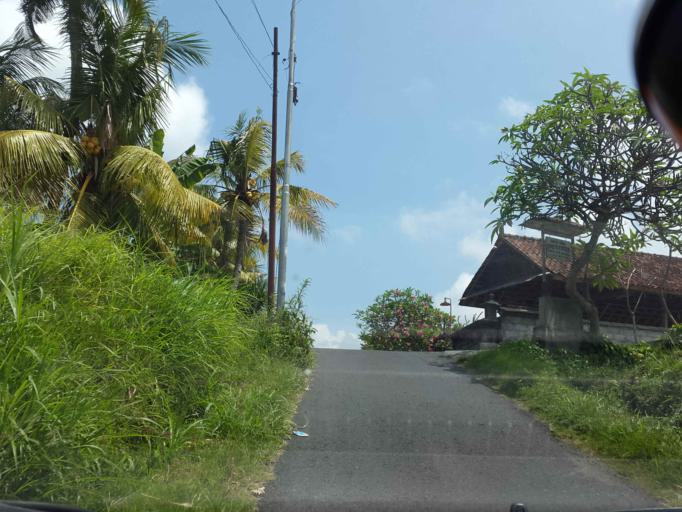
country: ID
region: Bali
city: Klungkung
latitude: -8.5554
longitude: 115.3853
